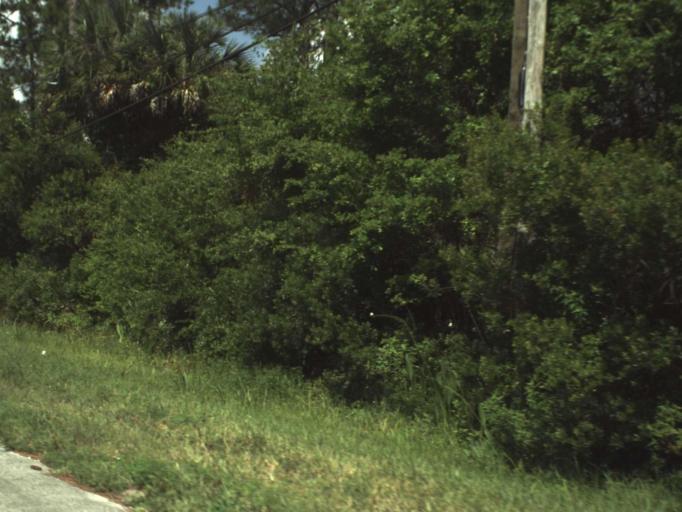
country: US
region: Florida
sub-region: Volusia County
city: Lake Helen
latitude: 28.9250
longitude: -81.1151
